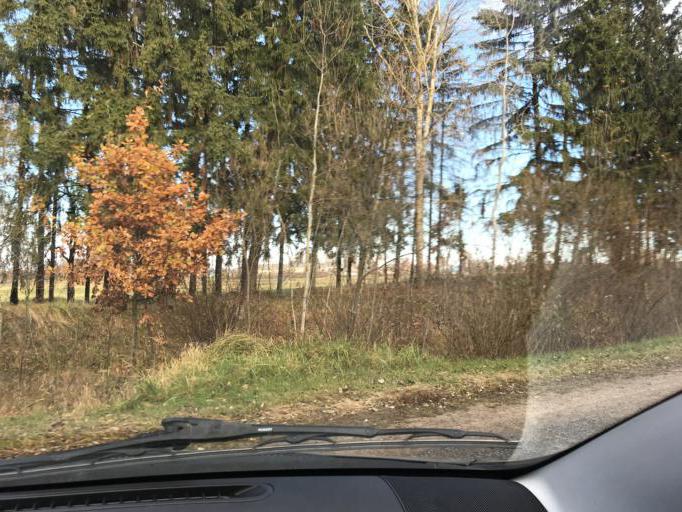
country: BY
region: Vitebsk
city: Haradok
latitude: 55.3704
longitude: 29.6219
